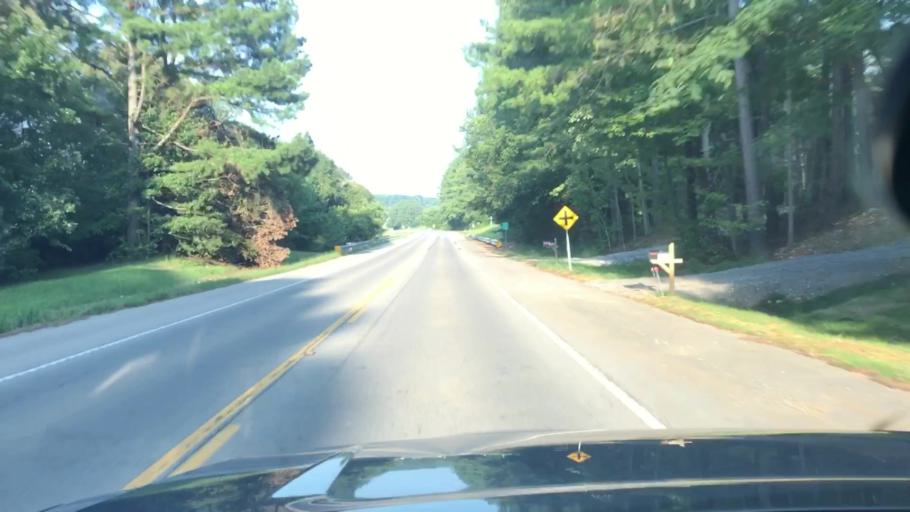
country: US
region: Tennessee
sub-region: Sumner County
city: Portland
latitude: 36.5787
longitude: -86.4292
